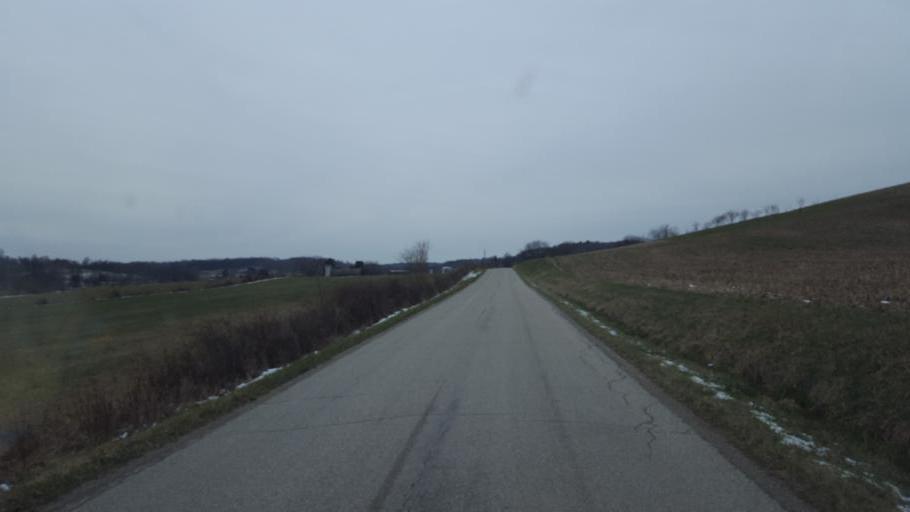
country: US
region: Ohio
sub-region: Sandusky County
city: Bellville
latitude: 40.5983
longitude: -82.5032
